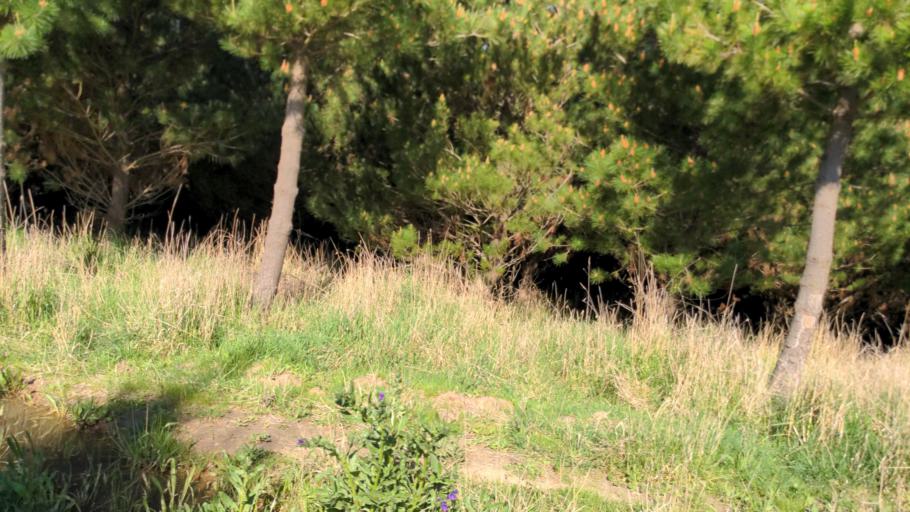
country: AU
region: New South Wales
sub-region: Blayney
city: Millthorpe
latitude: -33.4118
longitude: 149.3131
